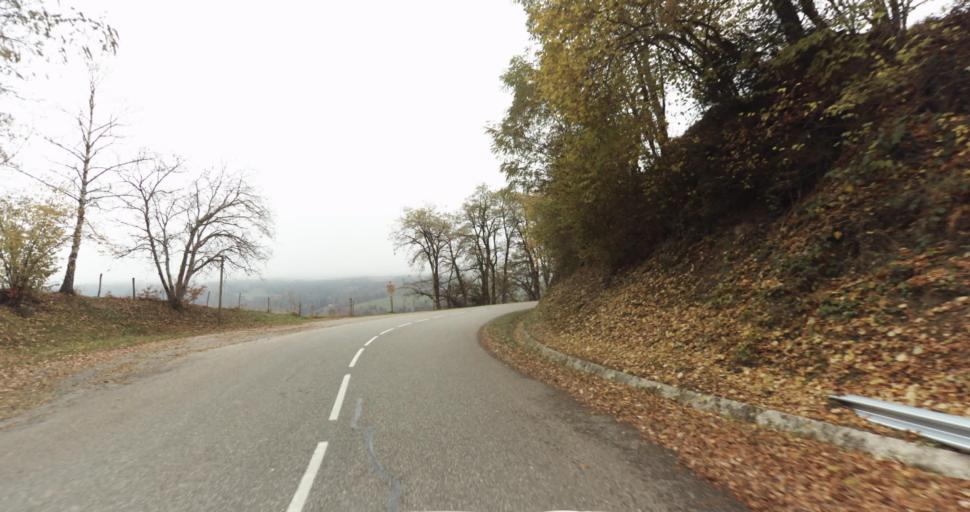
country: FR
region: Rhone-Alpes
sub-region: Departement de la Haute-Savoie
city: Saint-Jorioz
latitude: 45.7947
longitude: 6.1366
